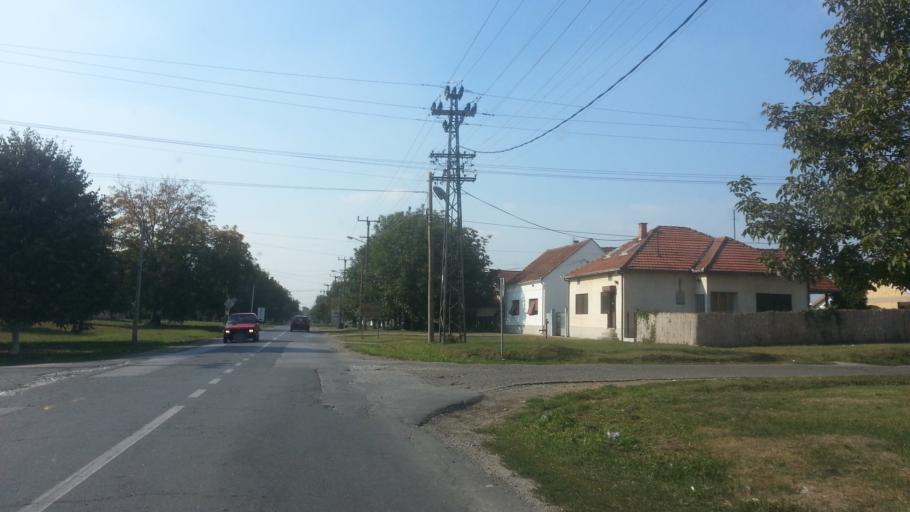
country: RS
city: Stari Banovci
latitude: 44.9838
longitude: 20.2738
